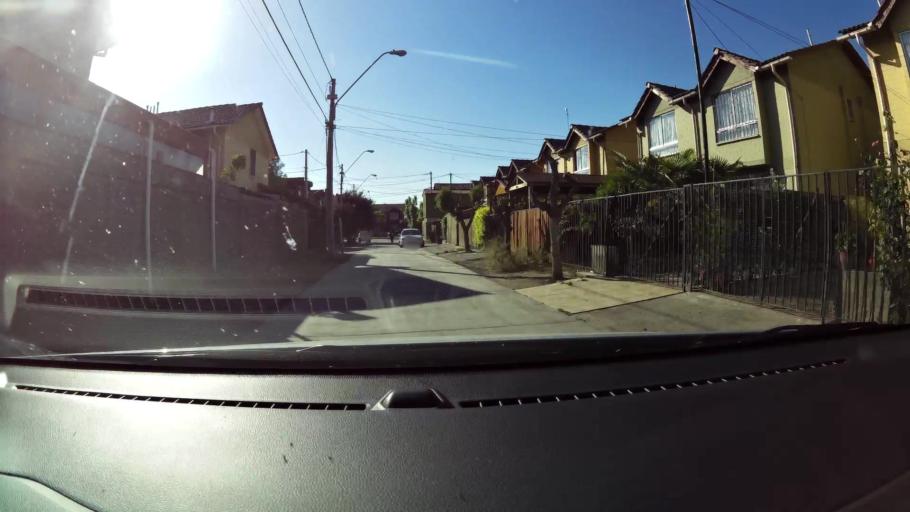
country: CL
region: Santiago Metropolitan
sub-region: Provincia de Maipo
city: San Bernardo
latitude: -33.5483
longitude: -70.7640
